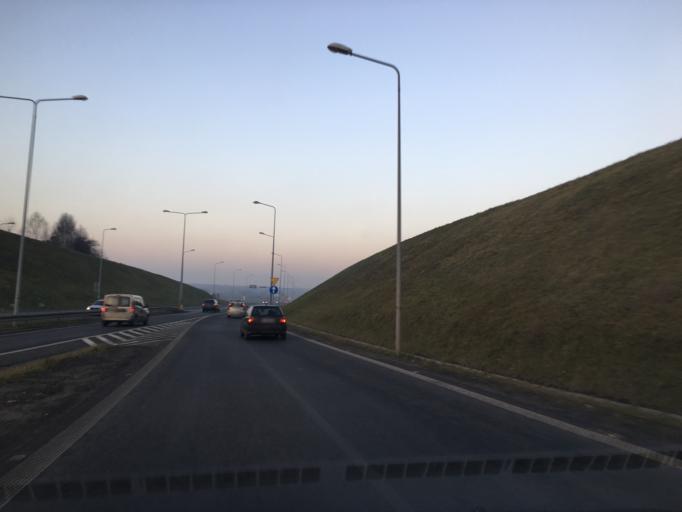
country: PL
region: Silesian Voivodeship
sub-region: Powiat tarnogorski
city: Radzionkow
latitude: 50.3556
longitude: 18.8678
